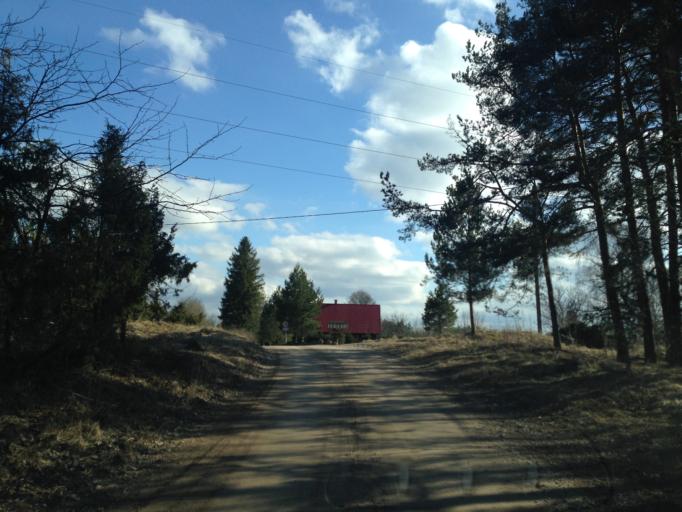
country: EE
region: Harju
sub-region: Keila linn
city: Keila
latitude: 59.1891
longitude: 24.4230
